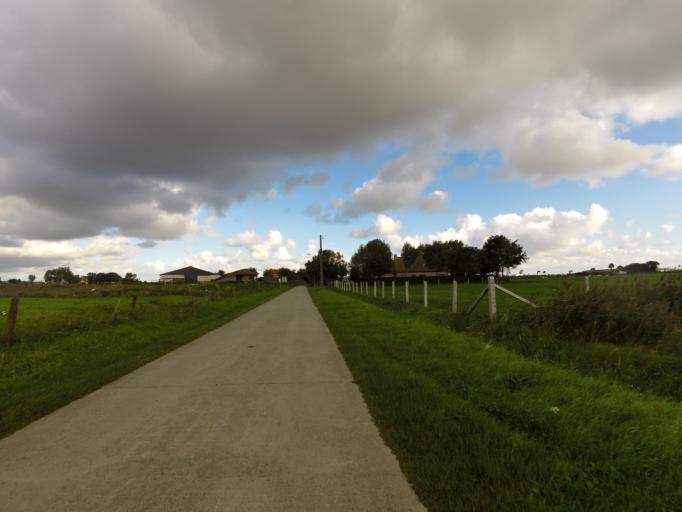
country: BE
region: Flanders
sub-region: Provincie West-Vlaanderen
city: Middelkerke
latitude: 51.1794
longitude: 2.8495
